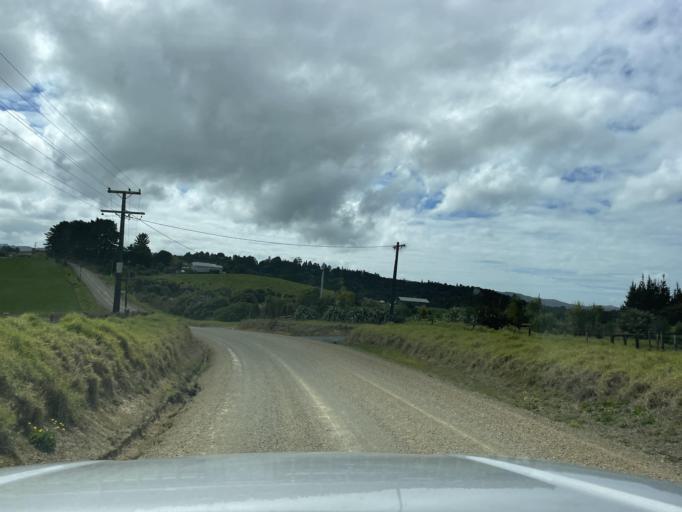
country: NZ
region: Auckland
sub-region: Auckland
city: Wellsford
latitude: -36.1423
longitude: 174.5403
